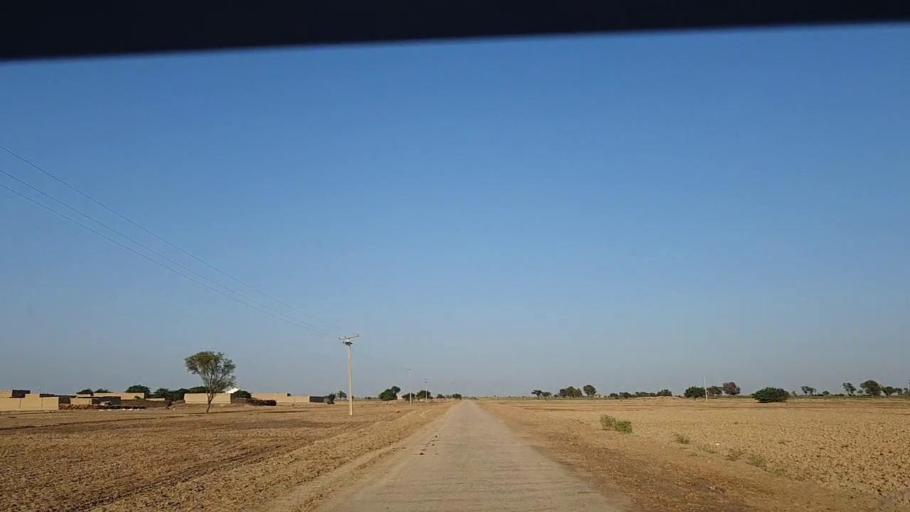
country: PK
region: Sindh
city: Johi
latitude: 26.7443
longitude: 67.6072
